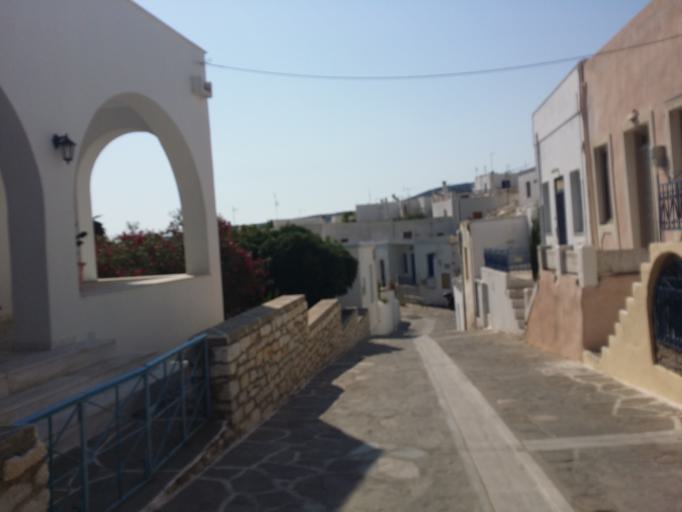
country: GR
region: South Aegean
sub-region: Nomos Kykladon
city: Paros
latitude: 37.0562
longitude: 25.2069
